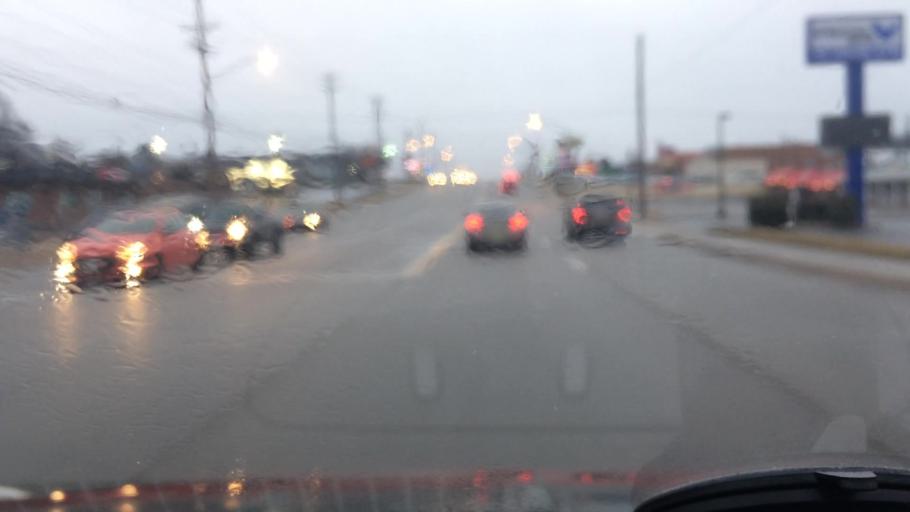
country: US
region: Missouri
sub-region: Greene County
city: Springfield
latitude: 37.1805
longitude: -93.2333
